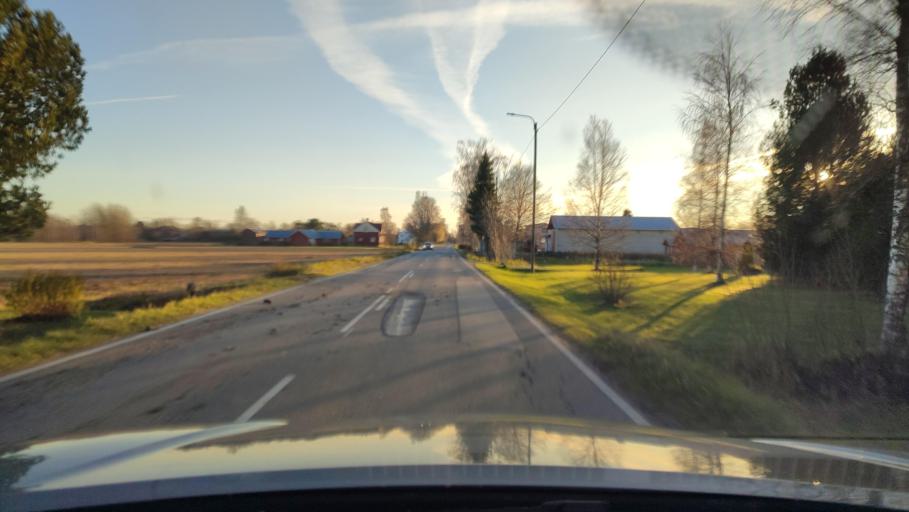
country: FI
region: Ostrobothnia
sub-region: Sydosterbotten
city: Naerpes
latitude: 62.6203
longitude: 21.4821
